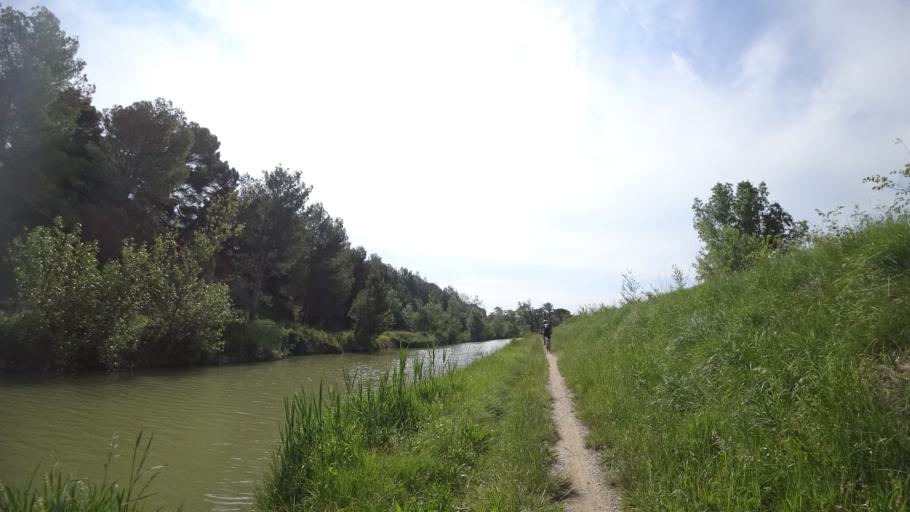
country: FR
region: Languedoc-Roussillon
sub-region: Departement de l'Herault
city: Olonzac
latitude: 43.2483
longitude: 2.7598
